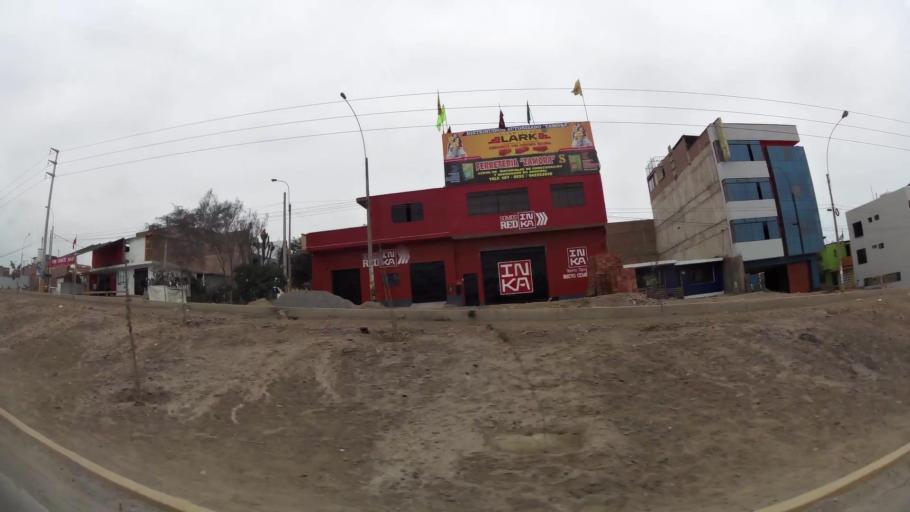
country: PE
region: Lima
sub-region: Lima
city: Surco
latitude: -12.2084
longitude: -76.9574
